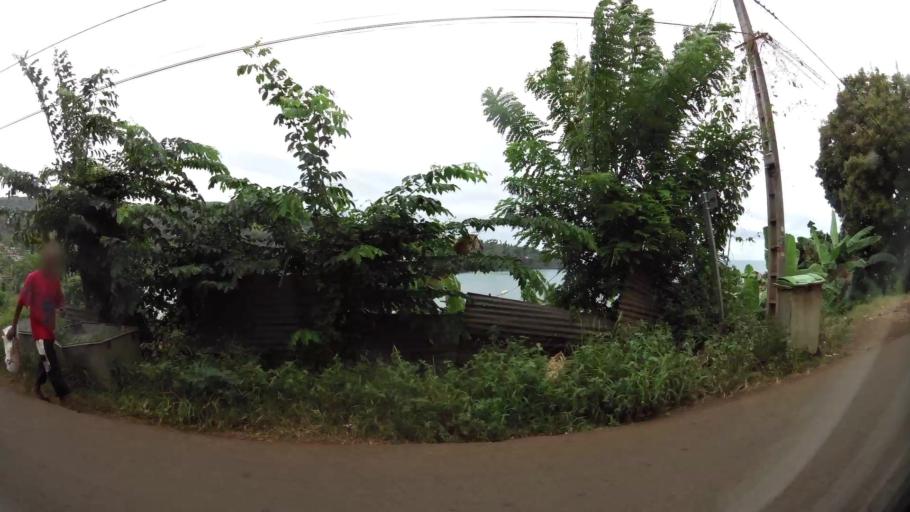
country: YT
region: Chiconi
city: Chiconi
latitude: -12.8373
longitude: 45.1161
